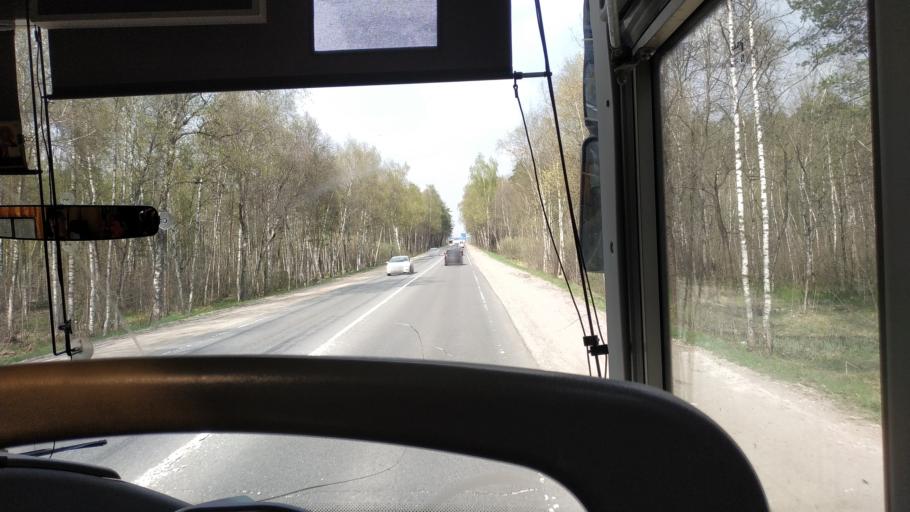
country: RU
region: Moskovskaya
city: Lytkarino
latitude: 55.6062
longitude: 37.9171
